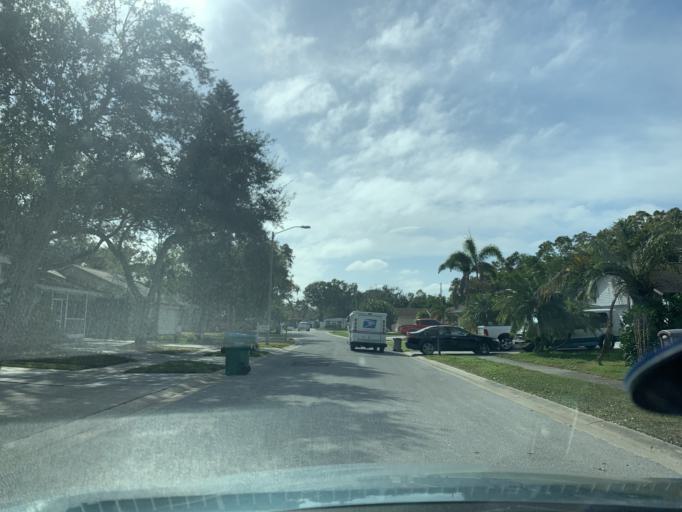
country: US
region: Florida
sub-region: Pinellas County
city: Largo
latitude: 27.8849
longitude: -82.7815
